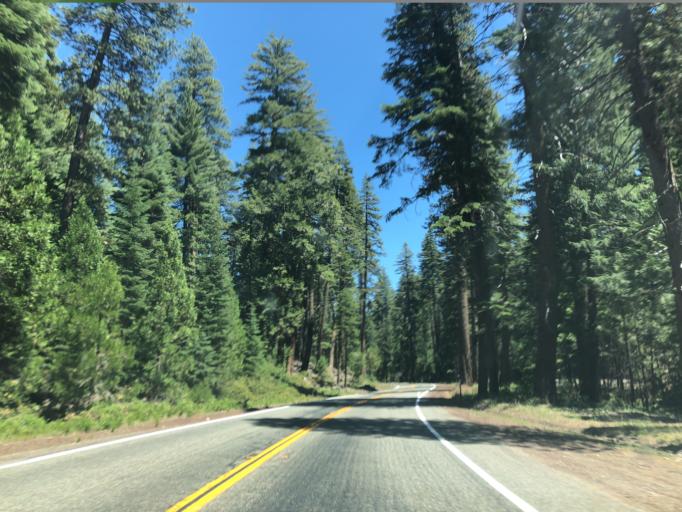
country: US
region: California
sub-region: Shasta County
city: Shingletown
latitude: 40.5329
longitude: -121.6257
